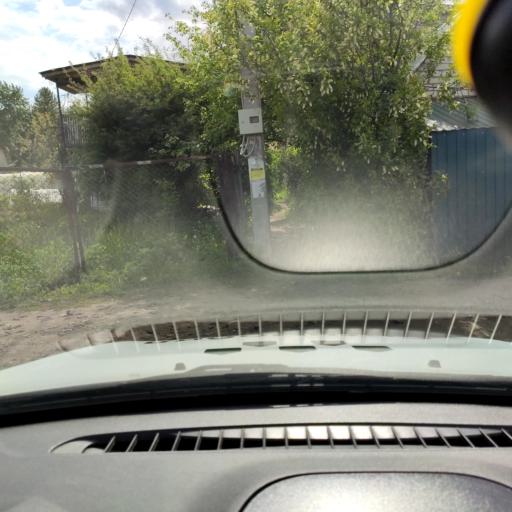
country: RU
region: Samara
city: Zhigulevsk
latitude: 53.5298
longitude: 49.5583
